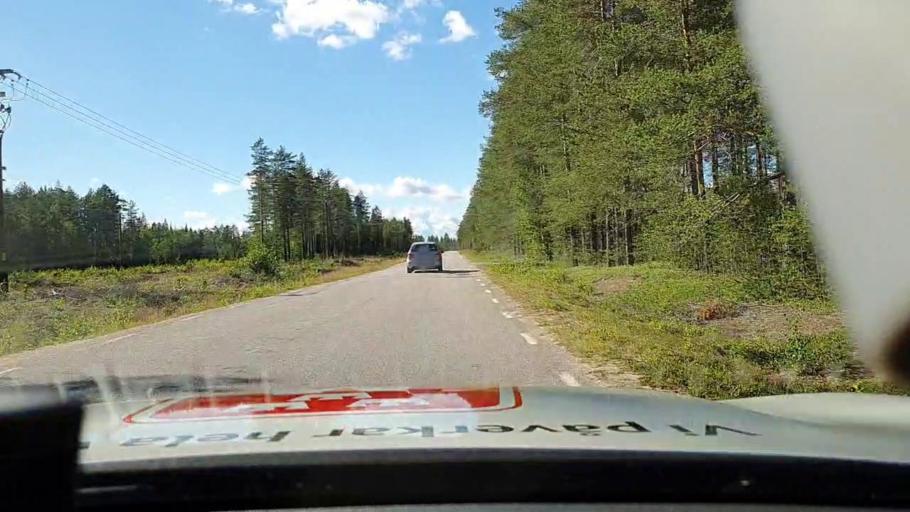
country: SE
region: Norrbotten
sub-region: Overkalix Kommun
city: OEverkalix
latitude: 66.2344
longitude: 22.9446
